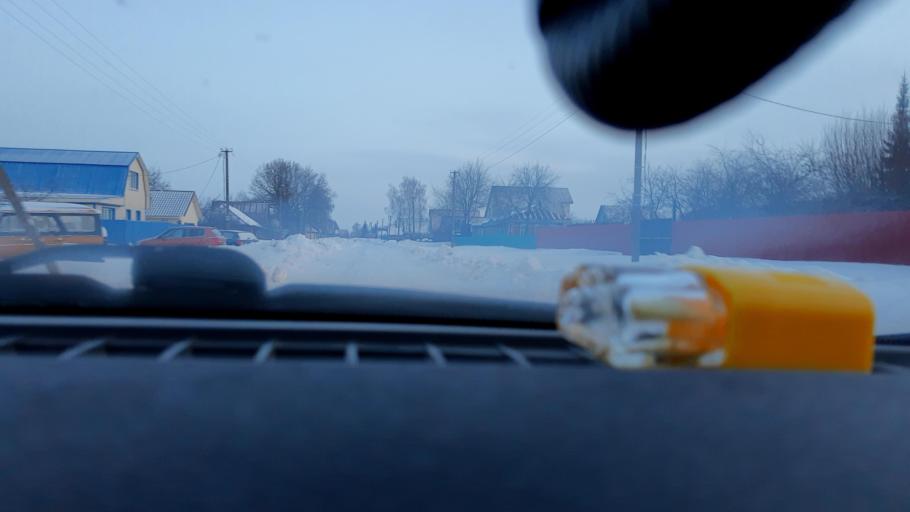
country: RU
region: Bashkortostan
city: Iglino
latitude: 54.7306
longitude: 56.3251
